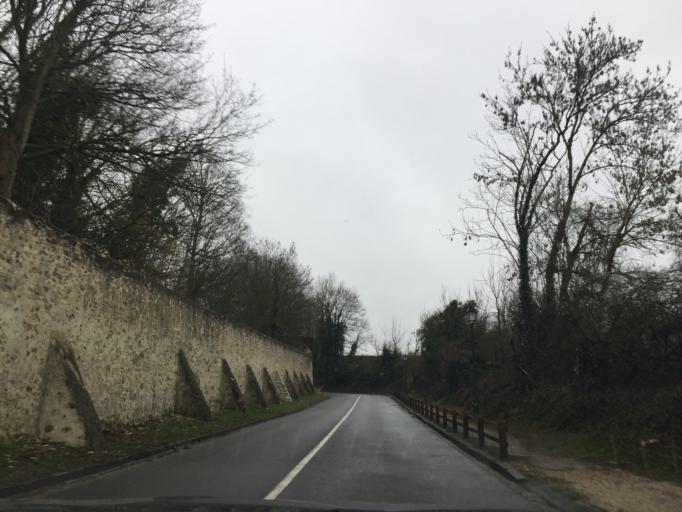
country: FR
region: Ile-de-France
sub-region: Departement de Seine-et-Marne
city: Coupvray
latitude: 48.8887
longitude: 2.7924
